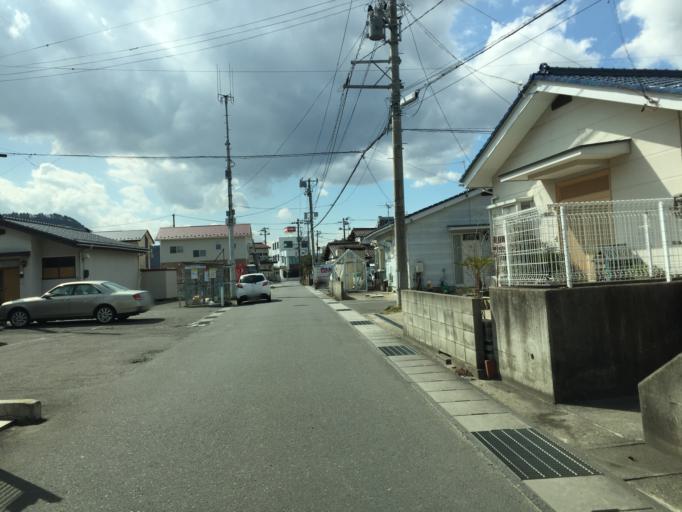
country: JP
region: Fukushima
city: Fukushima-shi
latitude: 37.7865
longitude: 140.4609
